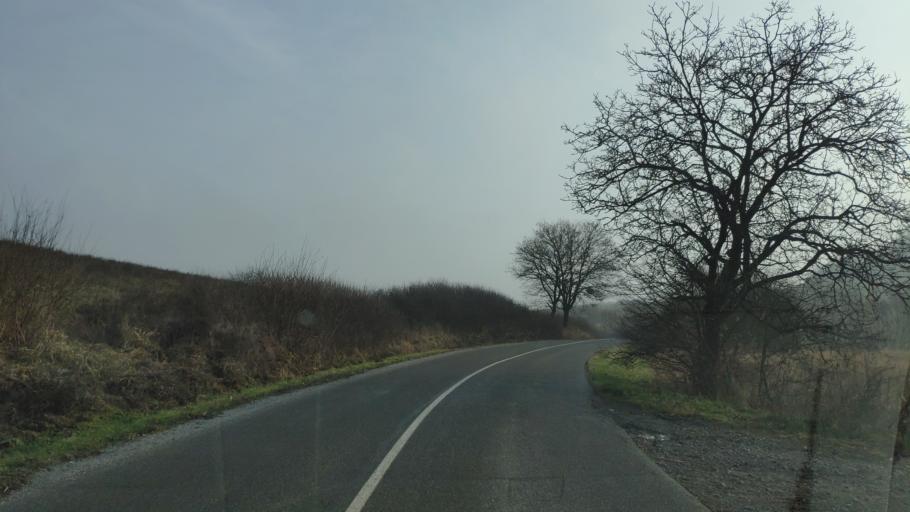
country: SK
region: Kosicky
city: Kosice
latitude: 48.7071
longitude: 21.3928
